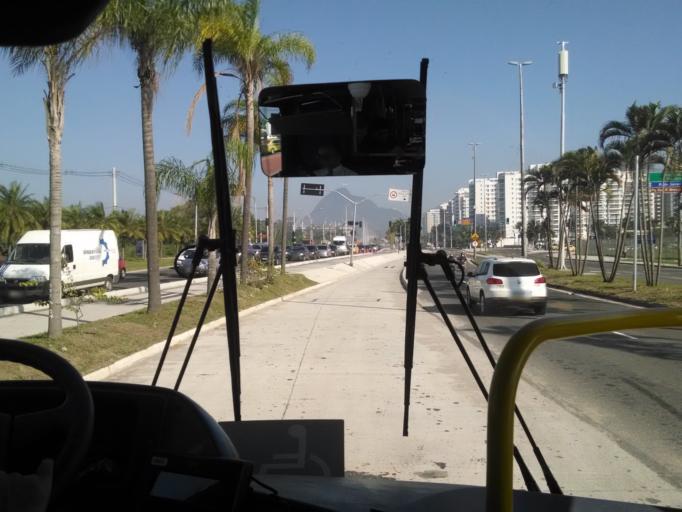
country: BR
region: Rio de Janeiro
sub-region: Sao Joao De Meriti
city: Sao Joao de Meriti
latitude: -22.9733
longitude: -43.3773
